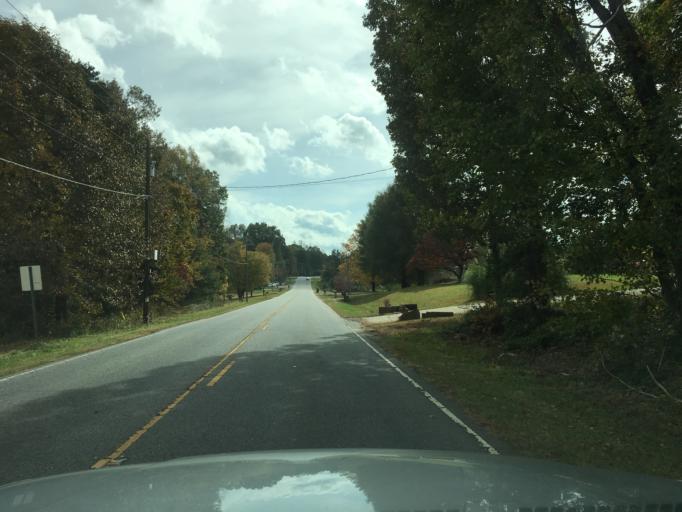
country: US
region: North Carolina
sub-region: Catawba County
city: Newton
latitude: 35.6682
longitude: -81.2726
